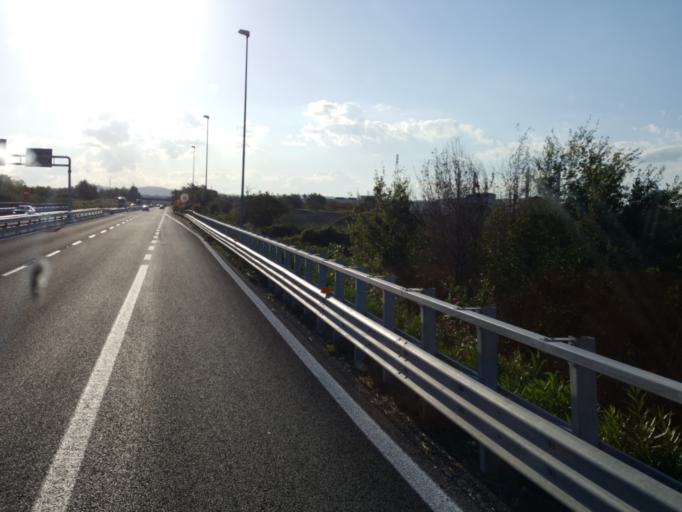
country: IT
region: Abruzzo
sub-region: Provincia di Chieti
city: Salvo Marina
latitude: 42.0558
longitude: 14.7685
